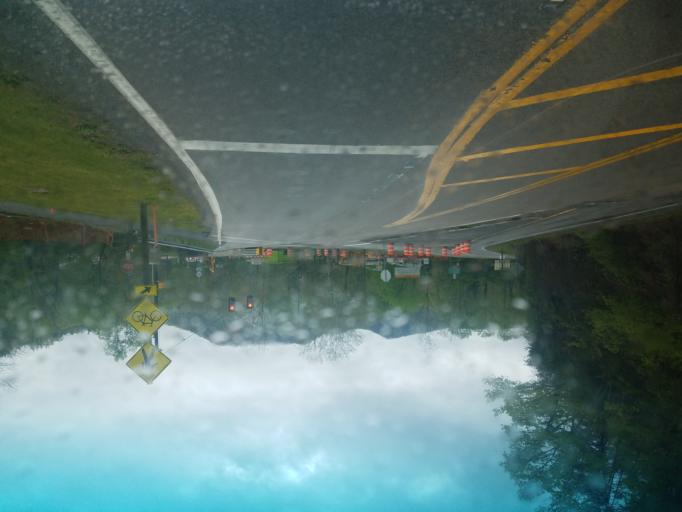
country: US
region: Tennessee
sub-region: Johnson County
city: Mountain City
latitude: 36.6260
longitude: -81.7713
